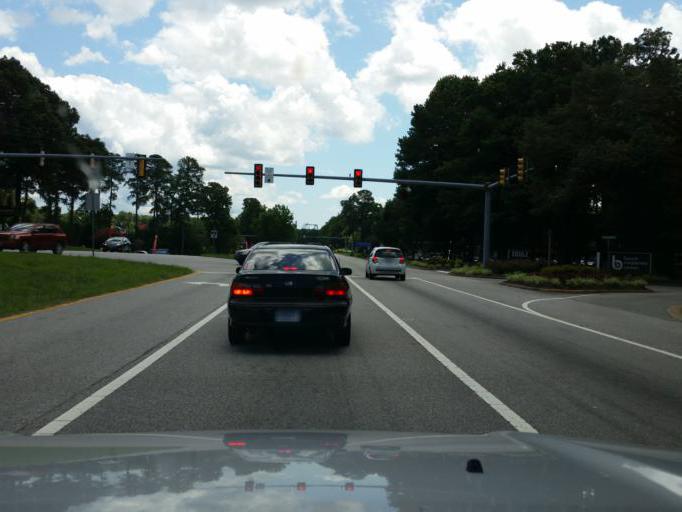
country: US
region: Virginia
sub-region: City of Williamsburg
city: Williamsburg
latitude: 37.2484
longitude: -76.6599
